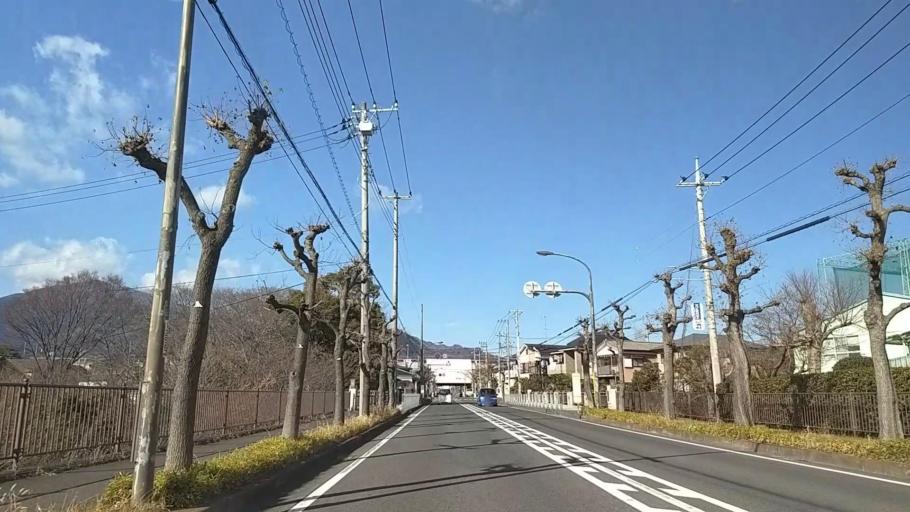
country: JP
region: Kanagawa
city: Isehara
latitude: 35.4037
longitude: 139.2958
